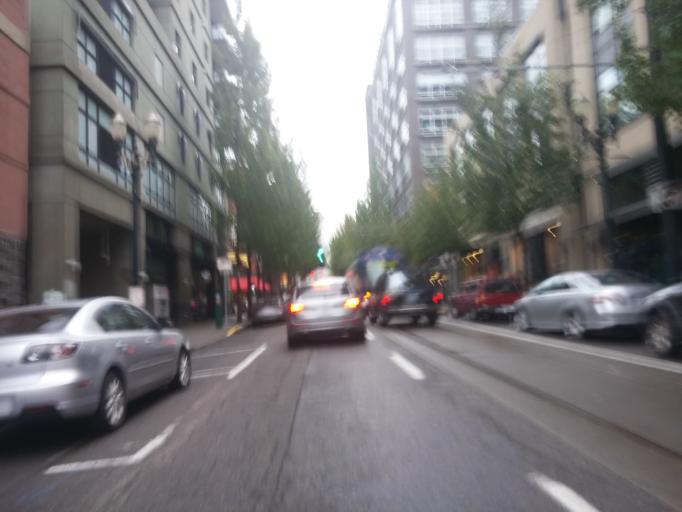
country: US
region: Oregon
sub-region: Multnomah County
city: Portland
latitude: 45.5244
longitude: -122.6823
